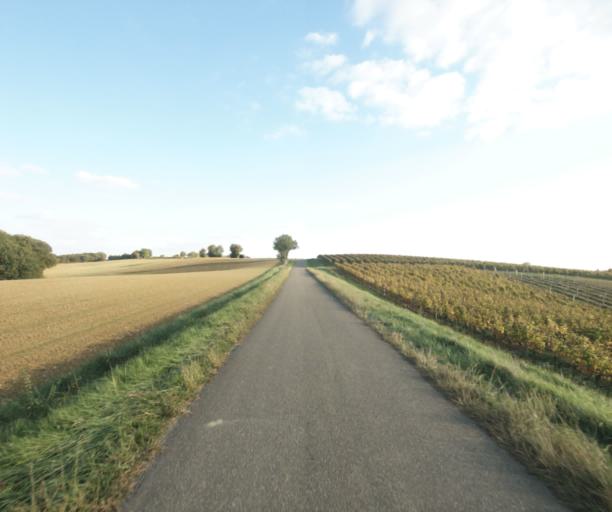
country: FR
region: Midi-Pyrenees
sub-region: Departement du Gers
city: Eauze
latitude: 43.7290
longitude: 0.1537
